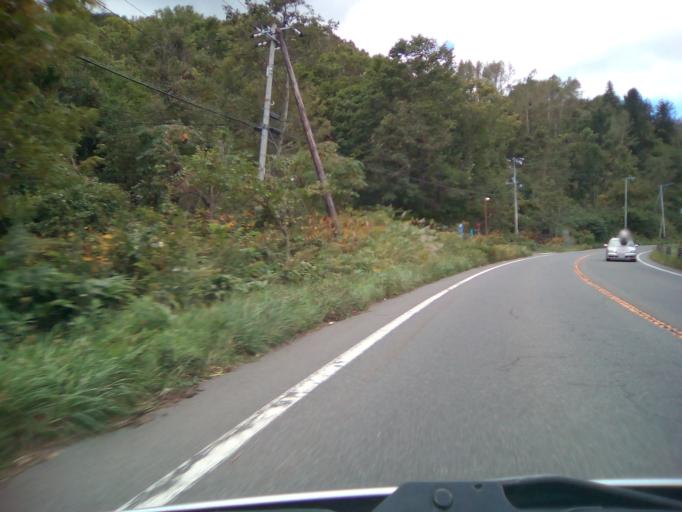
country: JP
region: Hokkaido
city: Date
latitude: 42.6026
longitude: 140.7728
